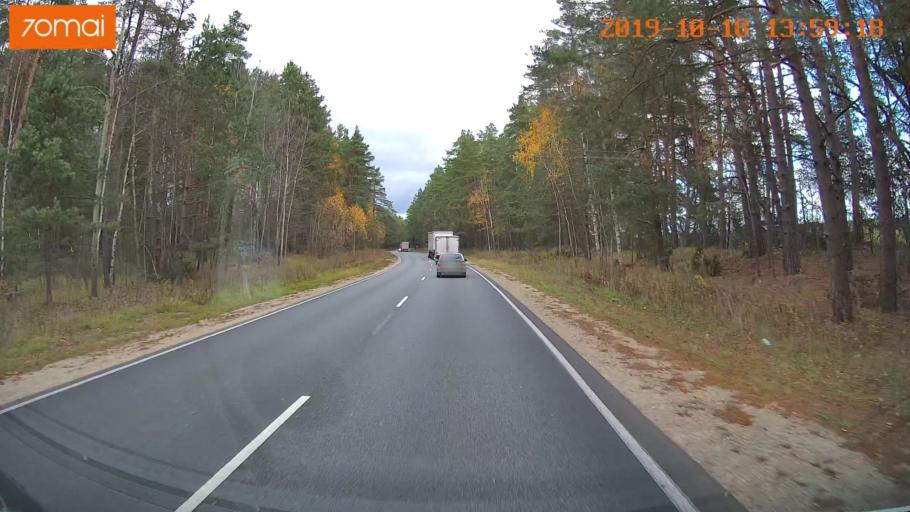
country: RU
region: Rjazan
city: Spas-Klepiki
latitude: 55.0929
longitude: 40.0623
